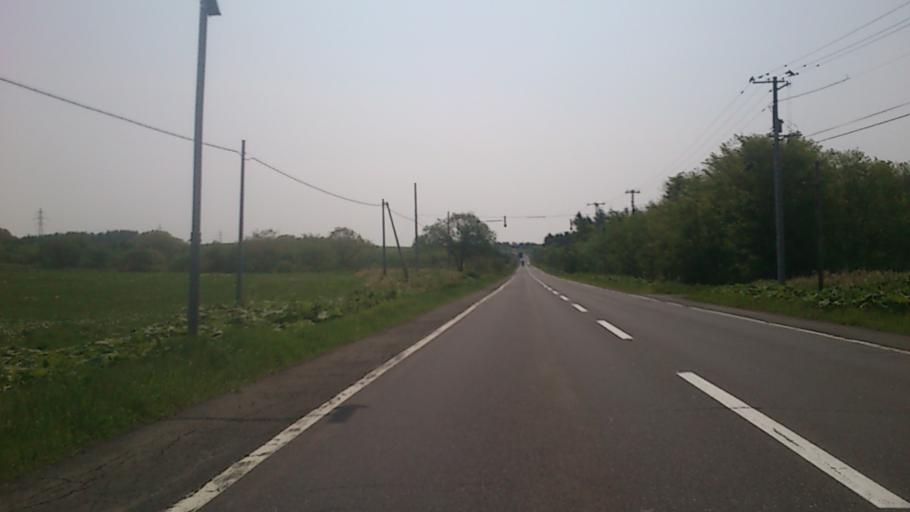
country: JP
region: Hokkaido
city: Kushiro
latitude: 43.4777
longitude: 144.5898
